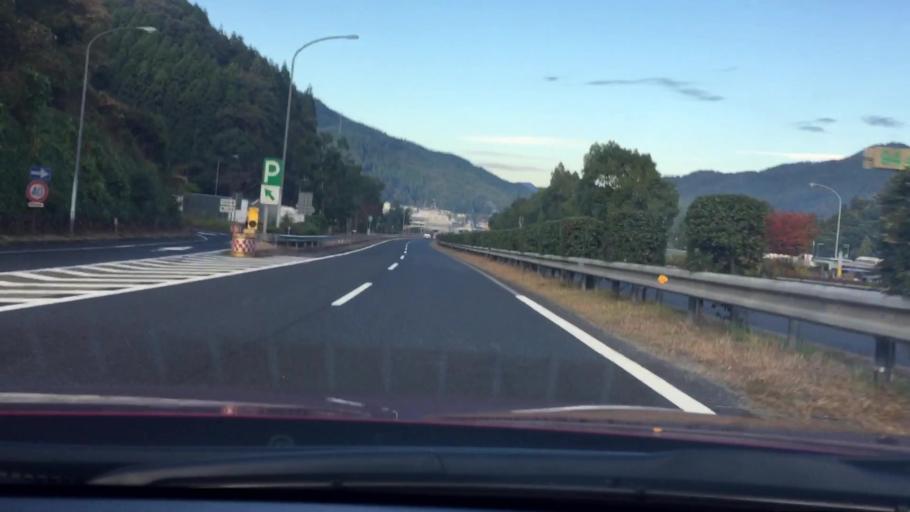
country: JP
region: Hyogo
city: Yamazakicho-nakabirose
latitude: 34.9842
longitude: 134.6051
